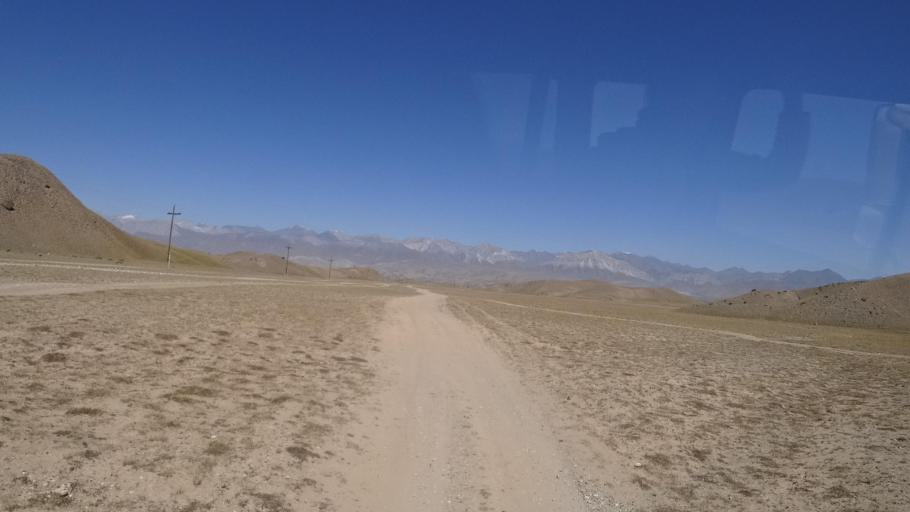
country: KG
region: Osh
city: Gul'cha
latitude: 39.5951
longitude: 72.8846
